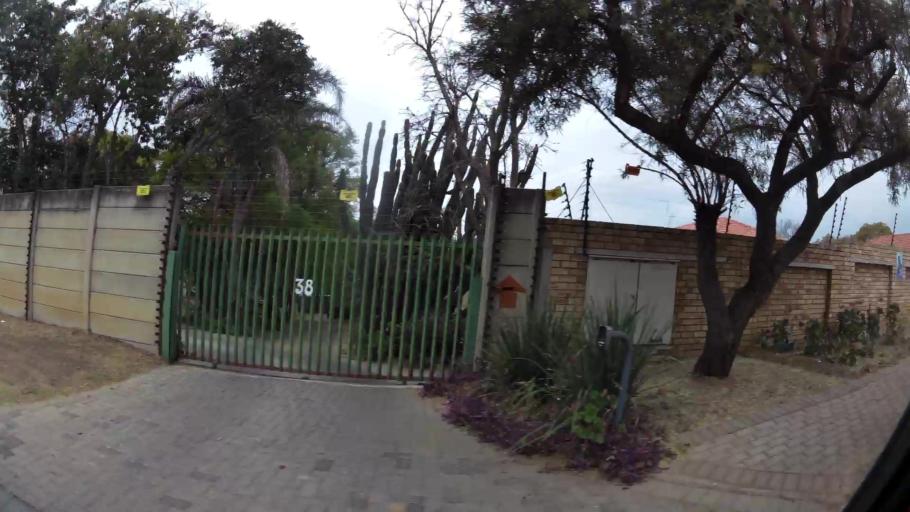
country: ZA
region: Gauteng
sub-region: City of Johannesburg Metropolitan Municipality
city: Roodepoort
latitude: -26.0972
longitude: 27.9103
